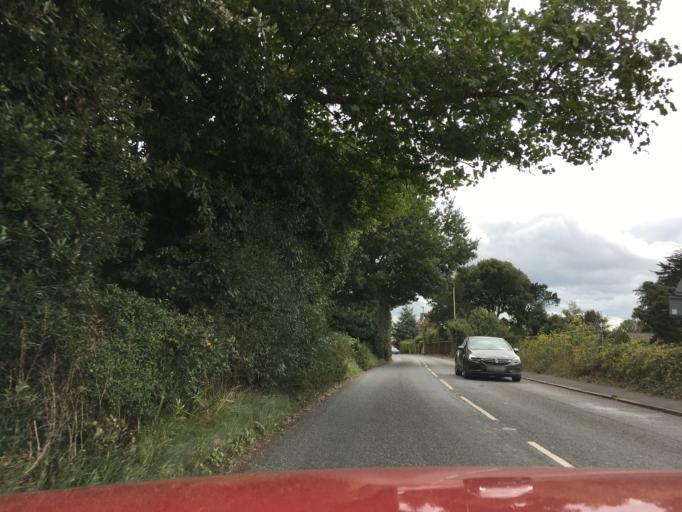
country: GB
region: England
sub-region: Devon
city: Starcross
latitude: 50.6315
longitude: -3.4500
